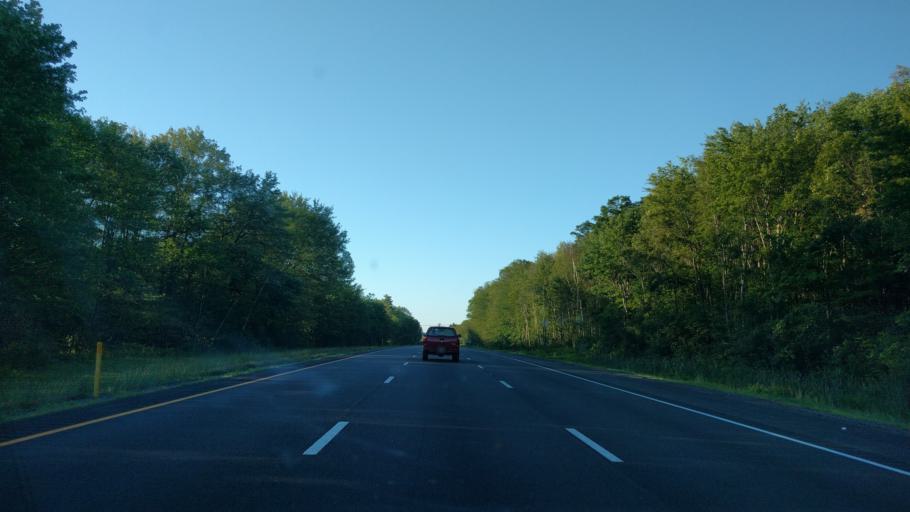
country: US
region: Massachusetts
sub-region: Worcester County
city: Milford
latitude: 42.1365
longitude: -71.4798
